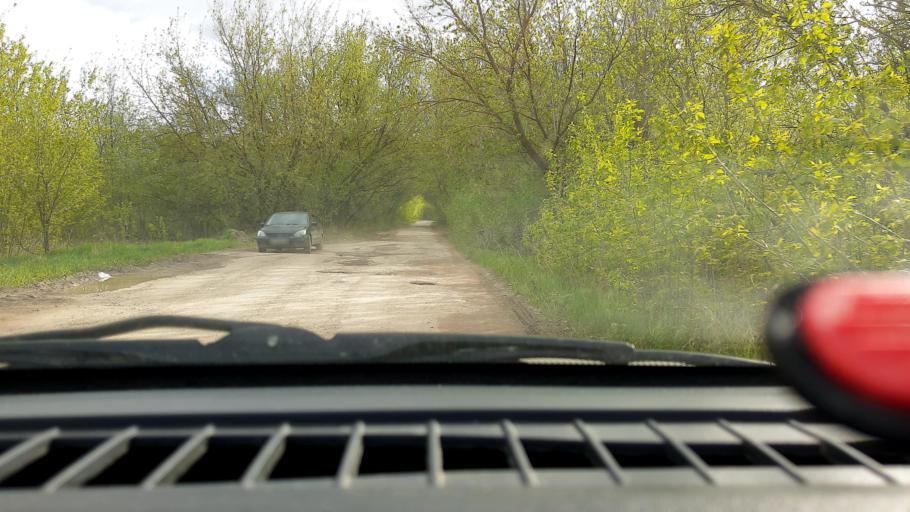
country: RU
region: Nizjnij Novgorod
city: Neklyudovo
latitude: 56.3921
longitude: 43.8448
